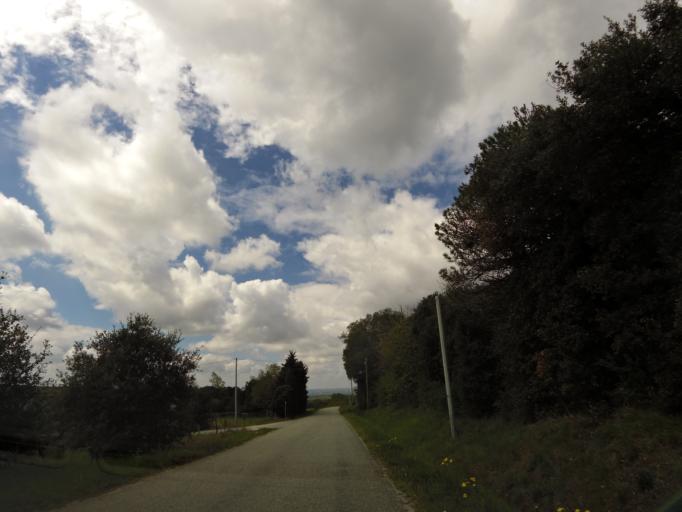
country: FR
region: Languedoc-Roussillon
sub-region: Departement de l'Aude
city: Villepinte
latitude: 43.3508
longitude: 2.0906
